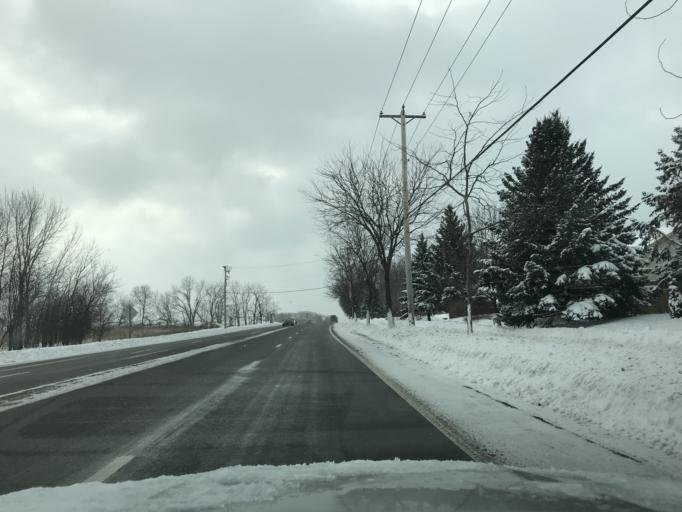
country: US
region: Wisconsin
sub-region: Dane County
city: Sun Prairie
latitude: 43.1627
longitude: -89.2851
